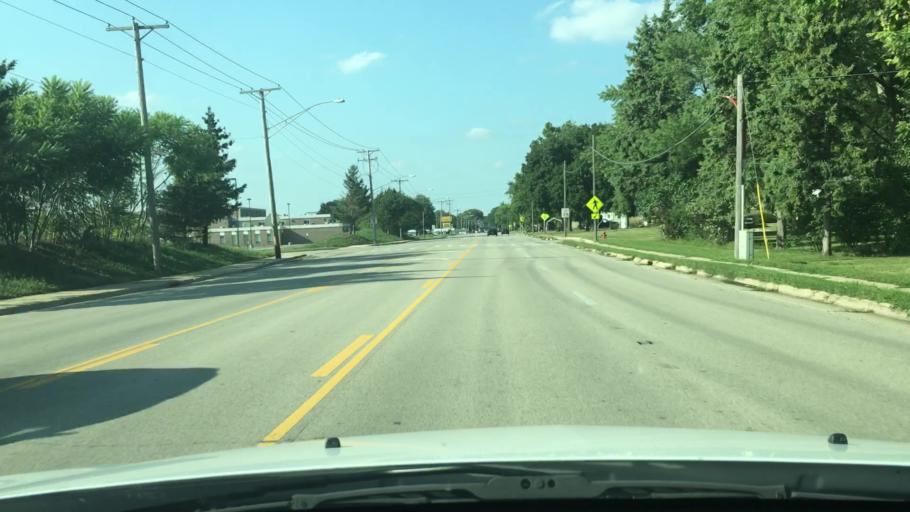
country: US
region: Illinois
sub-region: DeKalb County
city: DeKalb
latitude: 41.9089
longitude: -88.7535
